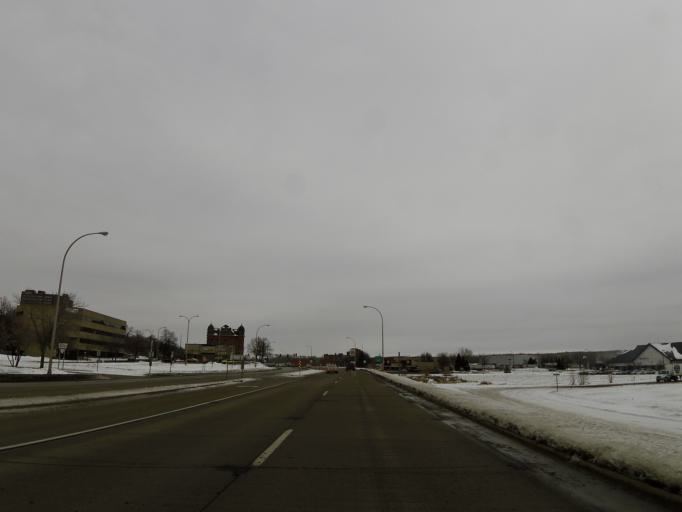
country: US
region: Minnesota
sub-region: Dakota County
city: South Saint Paul
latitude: 44.8908
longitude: -93.0333
